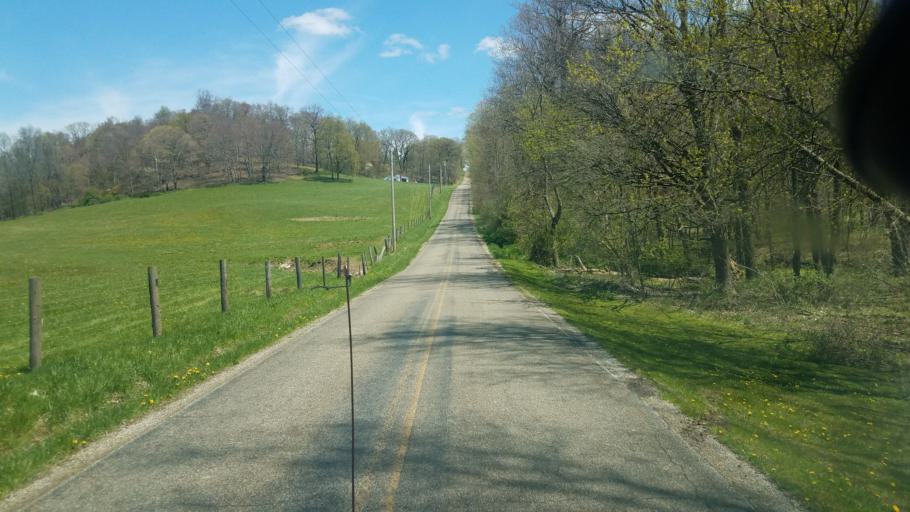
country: US
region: Ohio
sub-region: Richland County
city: Lincoln Heights
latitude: 40.7417
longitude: -82.4105
